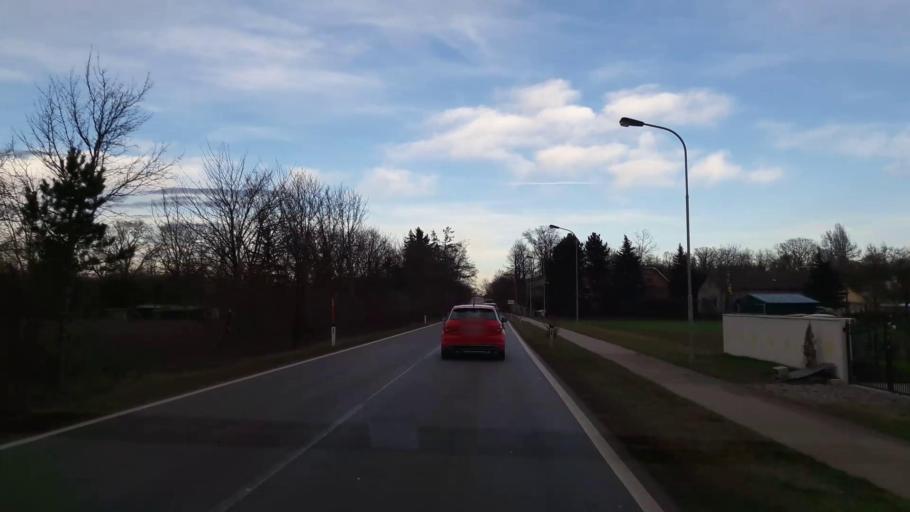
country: AT
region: Lower Austria
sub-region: Politischer Bezirk Baden
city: Ebreichsdorf
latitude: 47.9565
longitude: 16.4242
